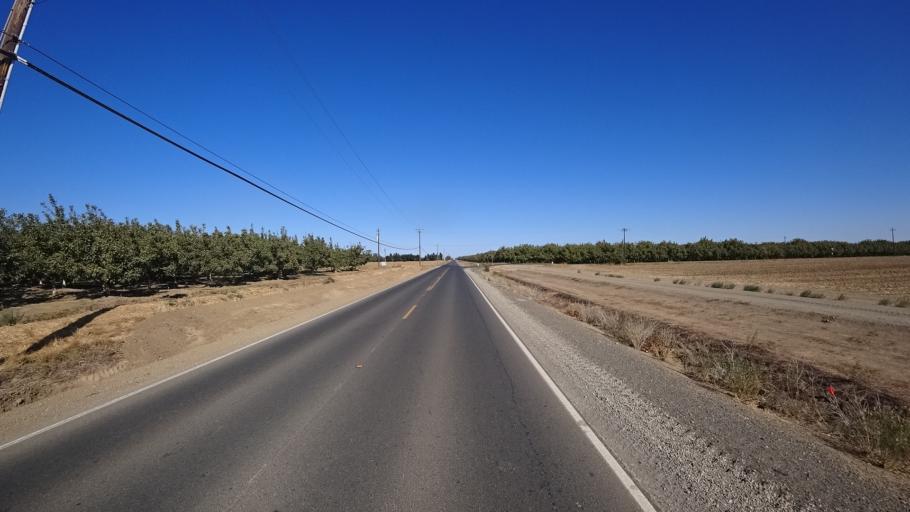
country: US
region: California
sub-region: Yolo County
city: Winters
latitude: 38.5609
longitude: -121.9713
